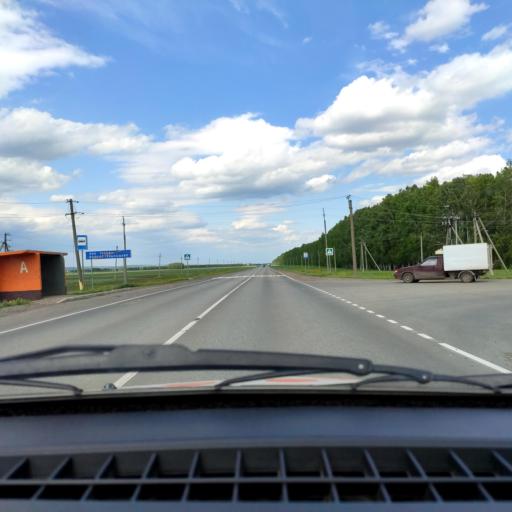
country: RU
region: Bashkortostan
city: Iglino
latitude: 55.0103
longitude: 56.4988
